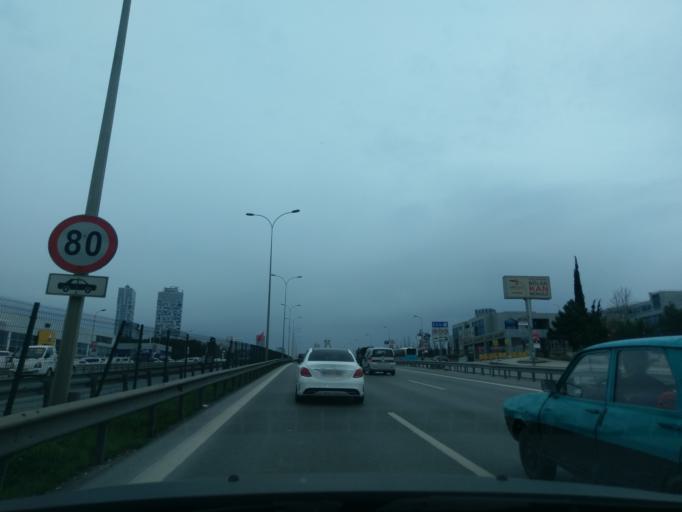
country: TR
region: Istanbul
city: Maltepe
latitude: 40.9172
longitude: 29.1764
